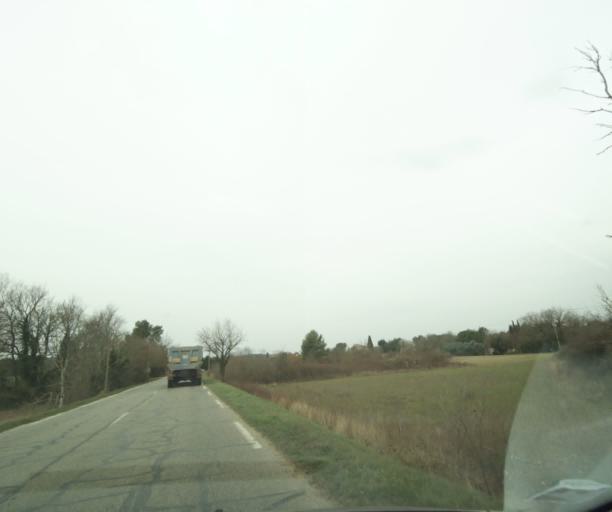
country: FR
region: Provence-Alpes-Cote d'Azur
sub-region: Departement des Bouches-du-Rhone
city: Peynier
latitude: 43.4476
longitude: 5.6569
